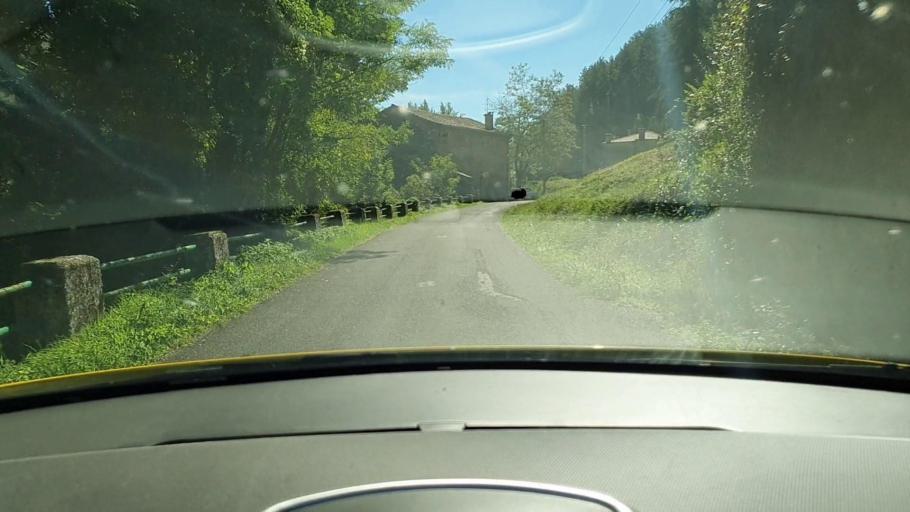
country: FR
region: Languedoc-Roussillon
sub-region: Departement du Gard
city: Le Vigan
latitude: 43.9671
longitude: 3.4371
